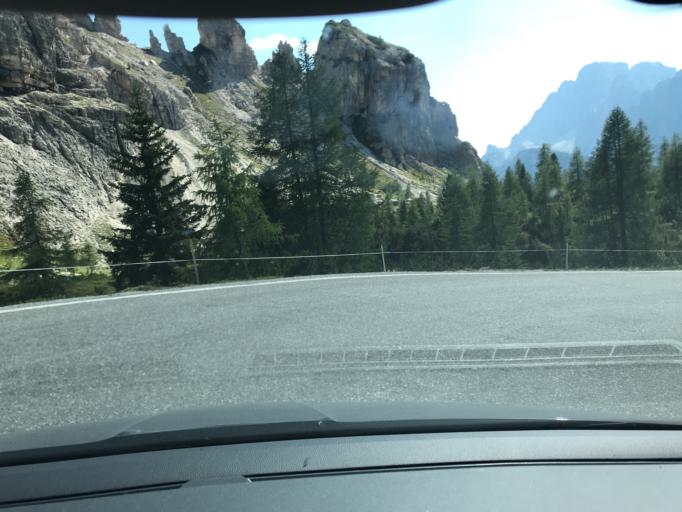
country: IT
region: Trentino-Alto Adige
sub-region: Bolzano
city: Sesto
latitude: 46.6069
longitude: 12.2907
